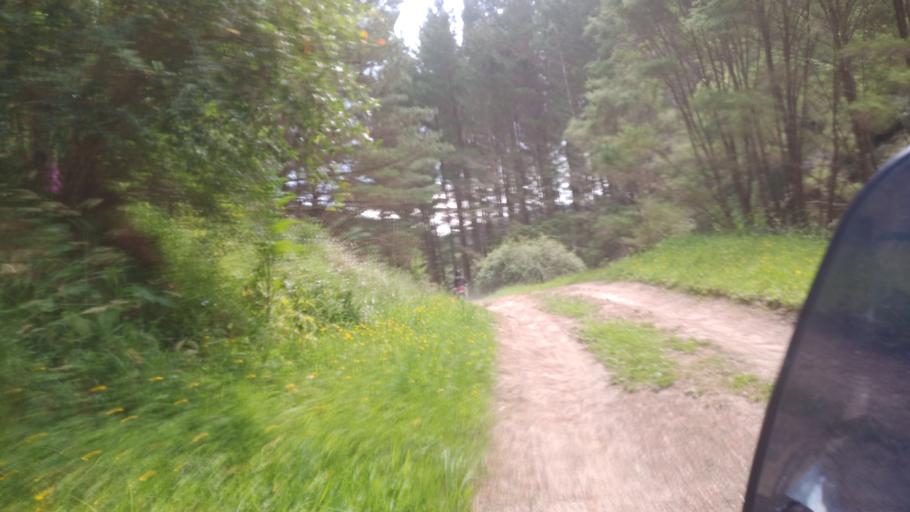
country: NZ
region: Gisborne
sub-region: Gisborne District
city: Gisborne
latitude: -38.4554
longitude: 177.9248
